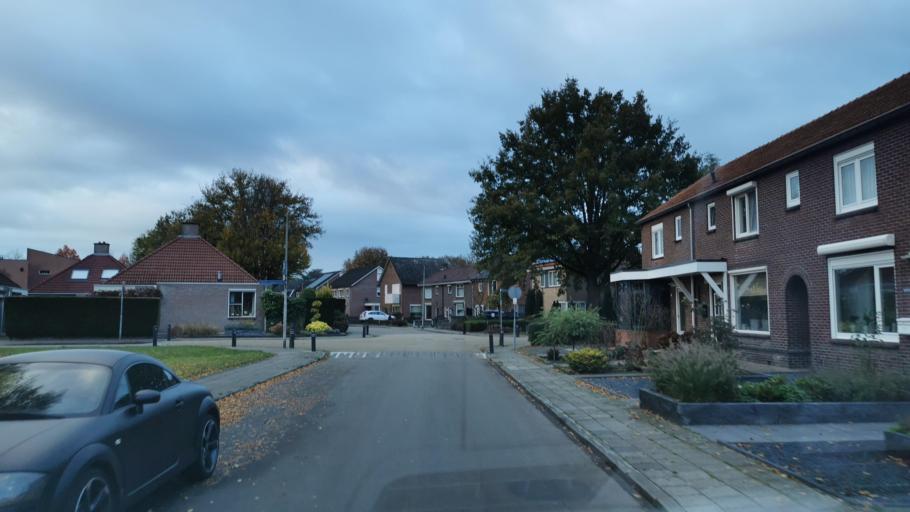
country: DE
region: North Rhine-Westphalia
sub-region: Regierungsbezirk Munster
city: Gronau
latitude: 52.2409
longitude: 7.0343
